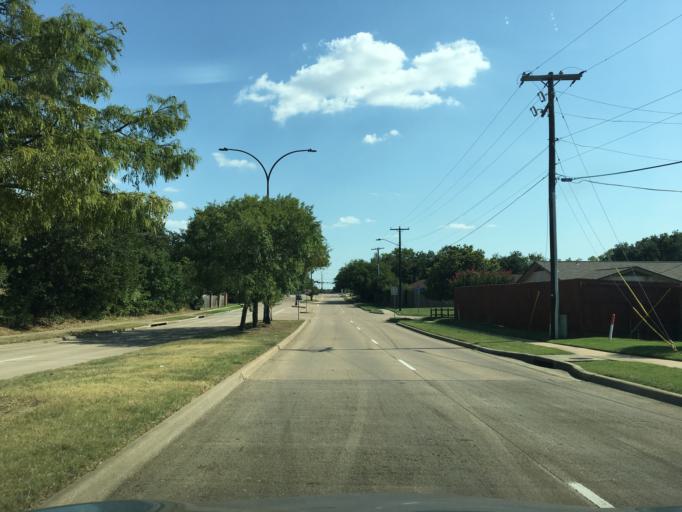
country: US
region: Texas
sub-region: Tarrant County
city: Dalworthington Gardens
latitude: 32.6725
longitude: -97.1497
